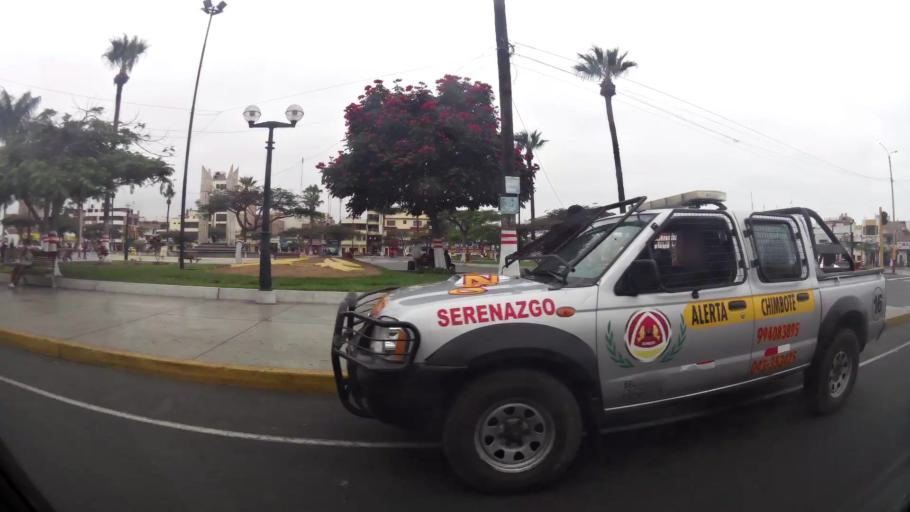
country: PE
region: Ancash
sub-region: Provincia de Santa
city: Chimbote
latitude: -9.0746
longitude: -78.5941
